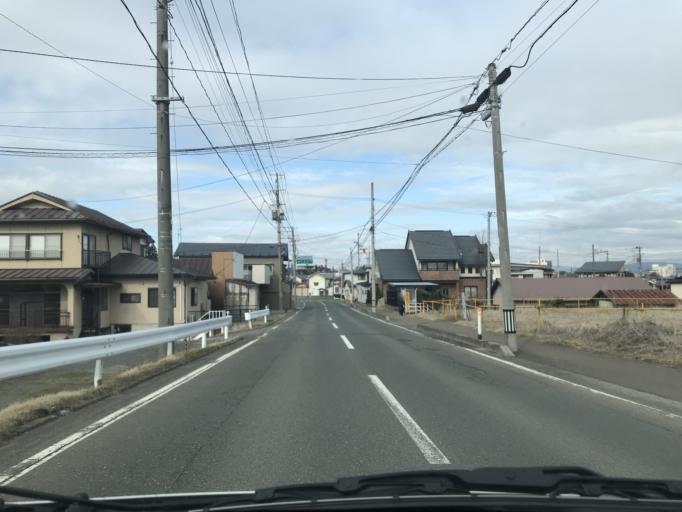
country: JP
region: Iwate
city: Hanamaki
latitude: 39.3798
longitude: 141.1065
